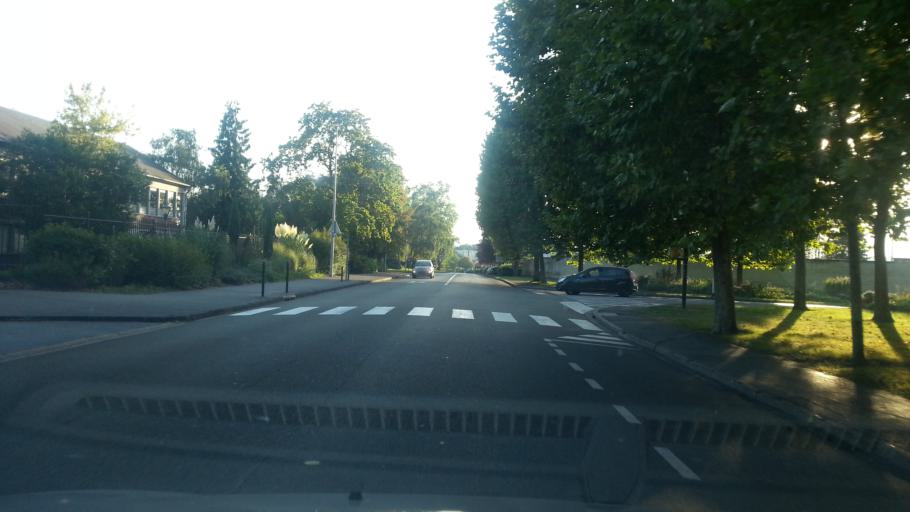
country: FR
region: Picardie
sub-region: Departement de l'Oise
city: Compiegne
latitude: 49.4011
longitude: 2.8162
